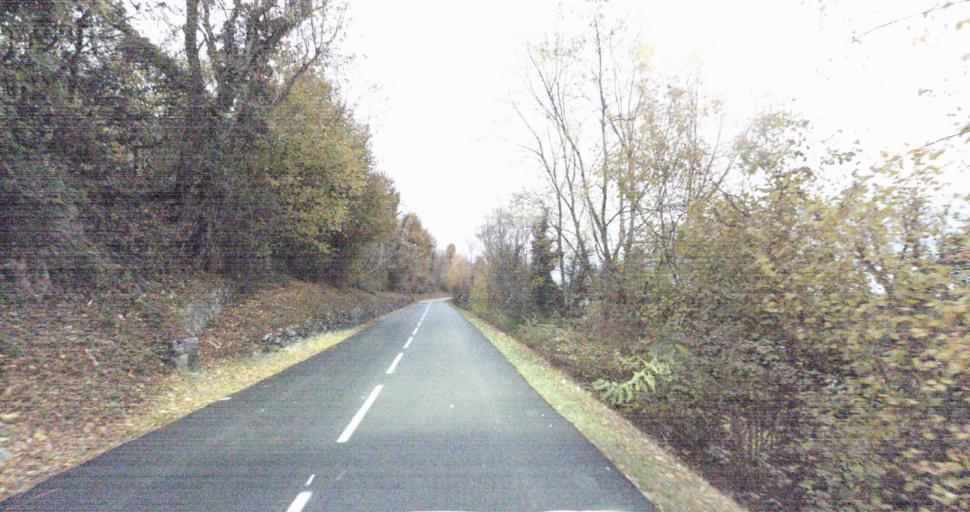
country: FR
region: Rhone-Alpes
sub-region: Departement de la Haute-Savoie
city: Sevrier
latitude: 45.8471
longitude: 6.1385
